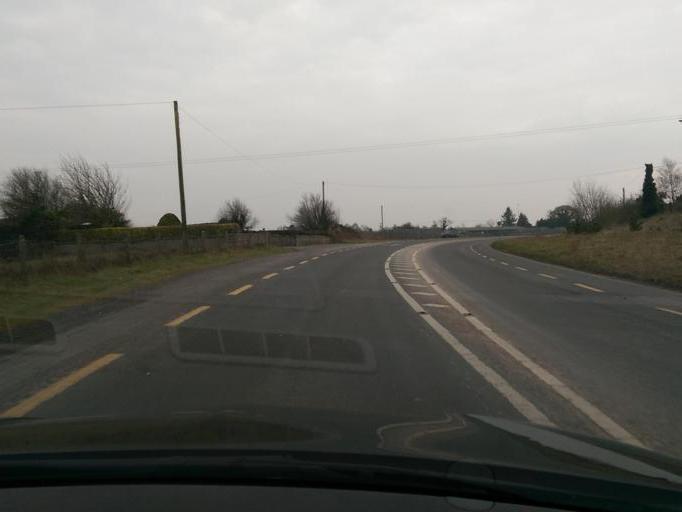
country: IE
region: Leinster
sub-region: An Iarmhi
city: Athlone
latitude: 53.4421
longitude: -7.8874
